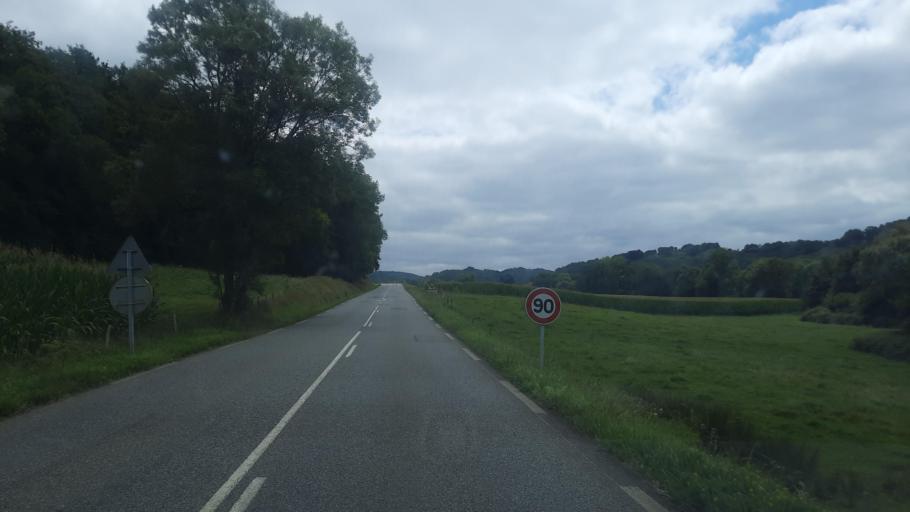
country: FR
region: Midi-Pyrenees
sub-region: Departement des Hautes-Pyrenees
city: Trie-sur-Baise
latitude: 43.3039
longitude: 0.2700
